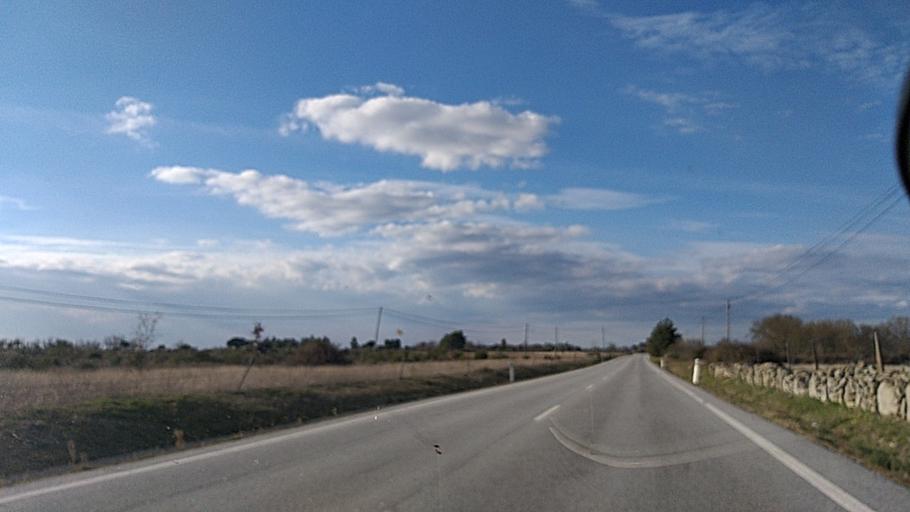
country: ES
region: Castille and Leon
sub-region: Provincia de Salamanca
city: Fuentes de Onoro
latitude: 40.6278
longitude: -6.8504
